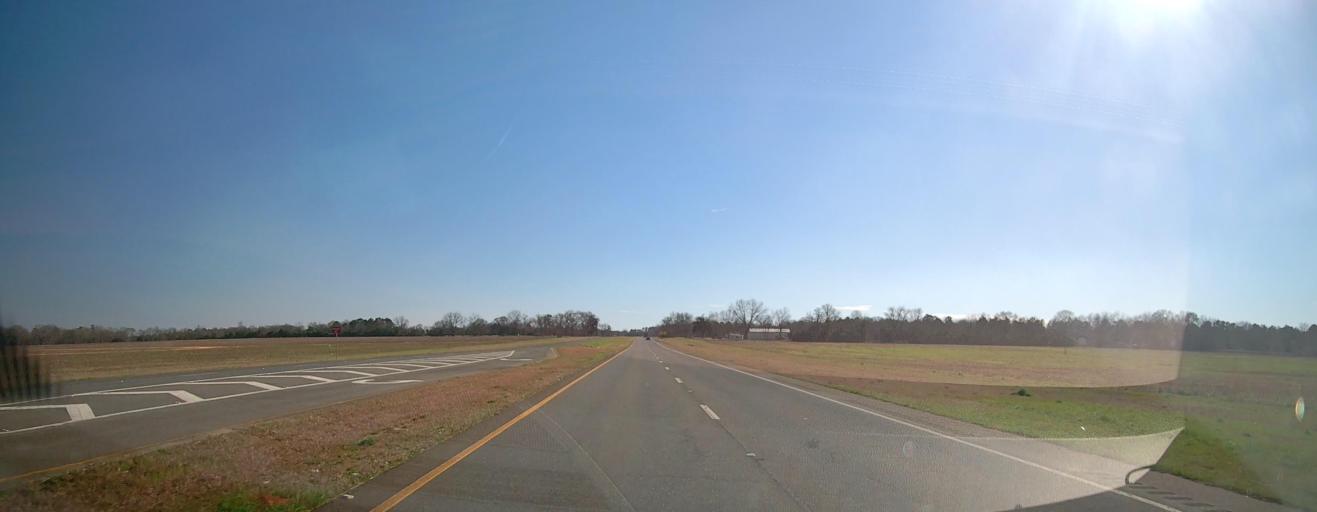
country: US
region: Georgia
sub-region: Schley County
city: Ellaville
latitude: 32.1721
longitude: -84.2689
